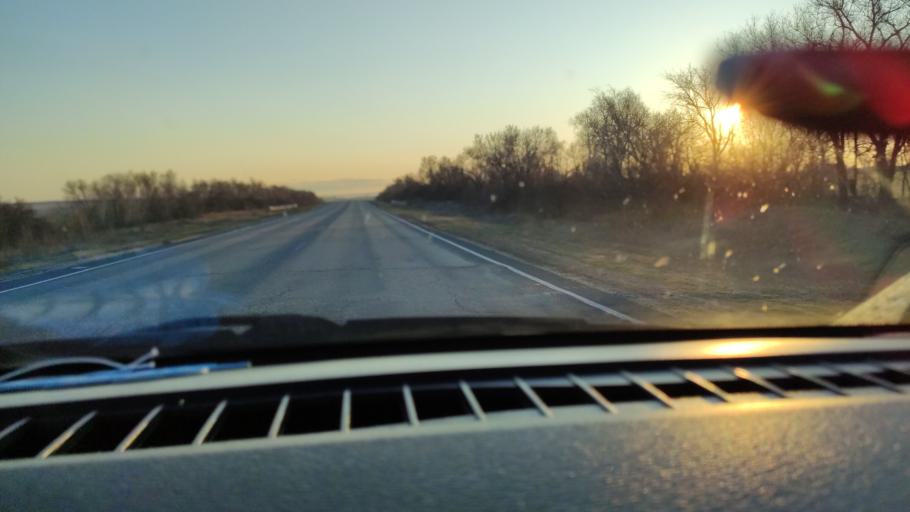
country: RU
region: Saratov
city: Sinodskoye
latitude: 51.9569
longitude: 46.6171
